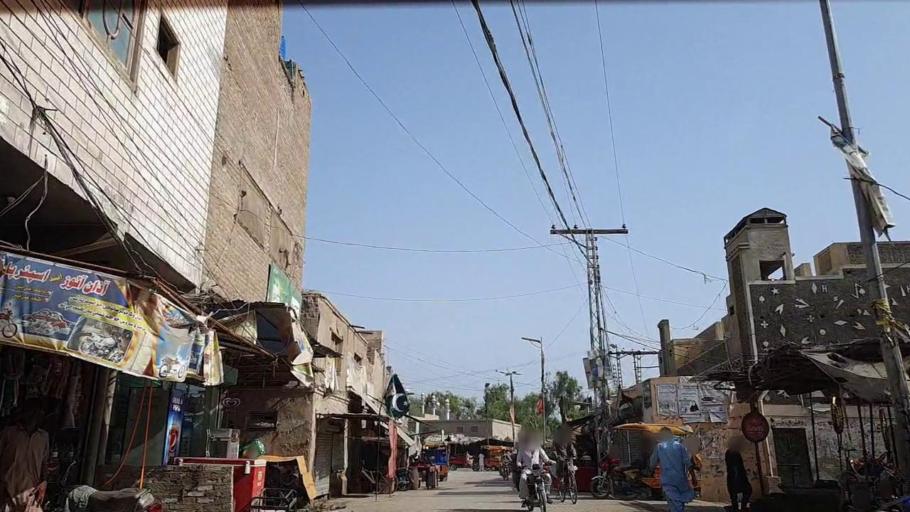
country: PK
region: Sindh
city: Kandiaro
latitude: 27.0588
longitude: 68.2079
